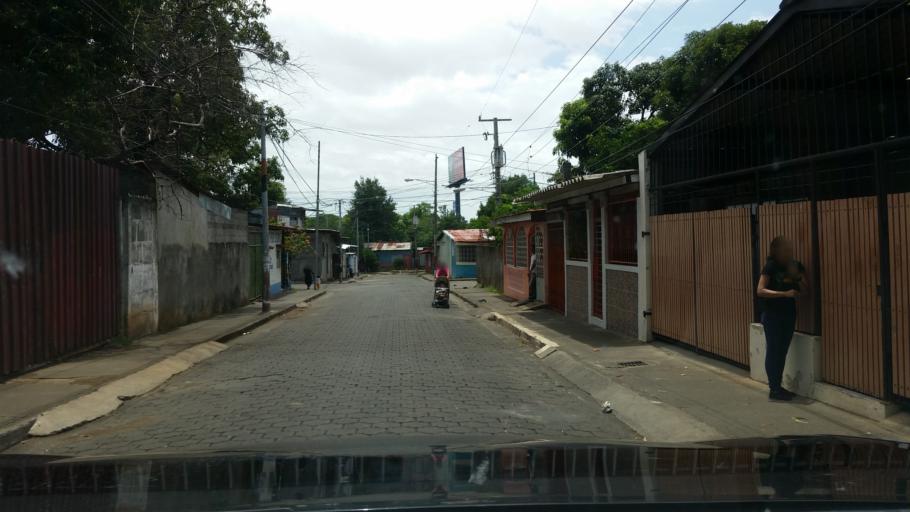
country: NI
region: Managua
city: Managua
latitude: 12.1309
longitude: -86.2581
